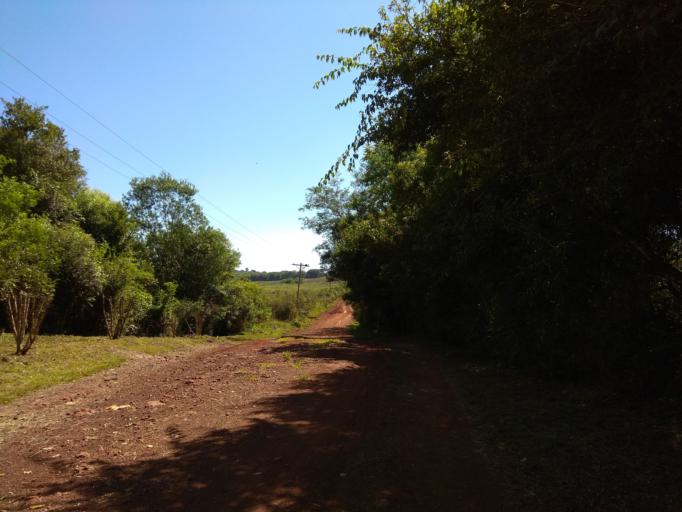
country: AR
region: Misiones
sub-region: Departamento de Apostoles
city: Apostoles
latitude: -27.9848
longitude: -55.7836
